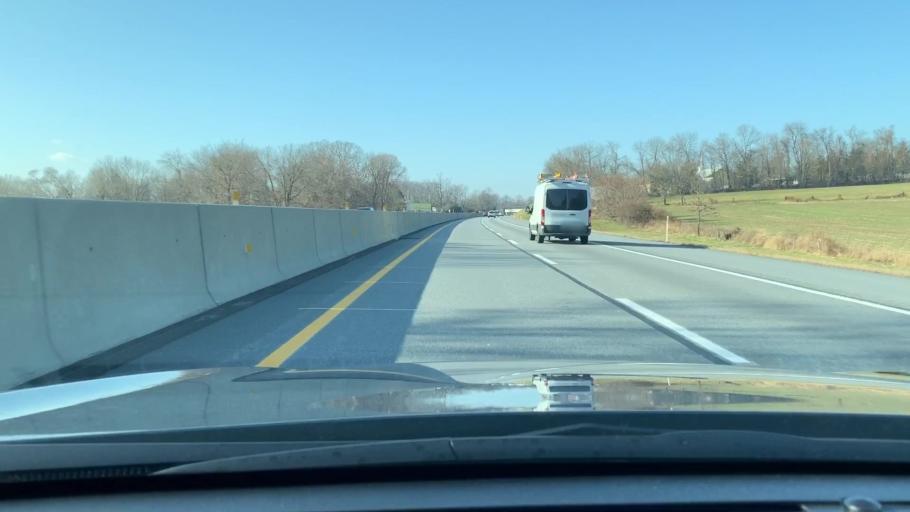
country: US
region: Pennsylvania
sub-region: Lancaster County
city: Elizabethtown
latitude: 40.2075
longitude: -76.6497
